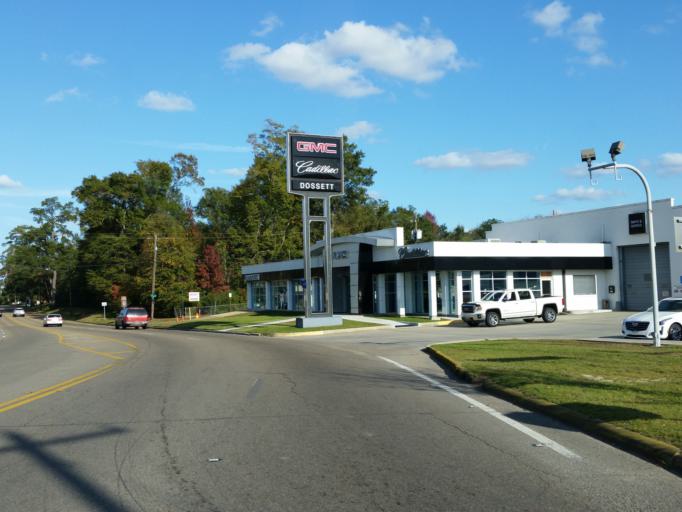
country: US
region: Mississippi
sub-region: Forrest County
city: Hattiesburg
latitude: 31.3170
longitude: -89.3016
